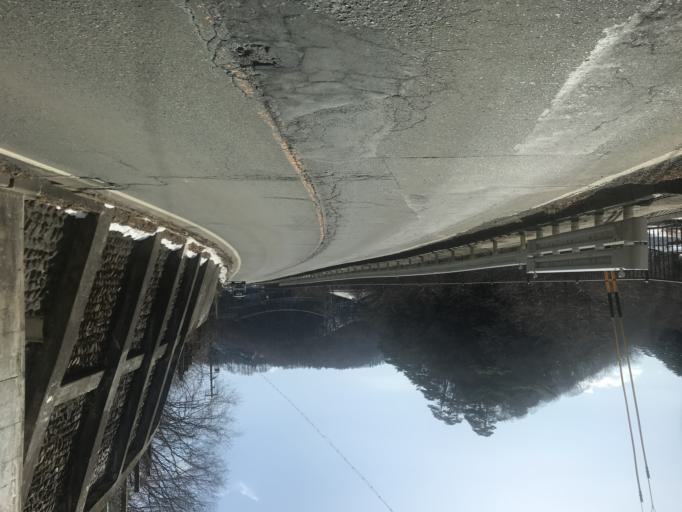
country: JP
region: Nagano
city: Saku
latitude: 36.0108
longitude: 138.4932
